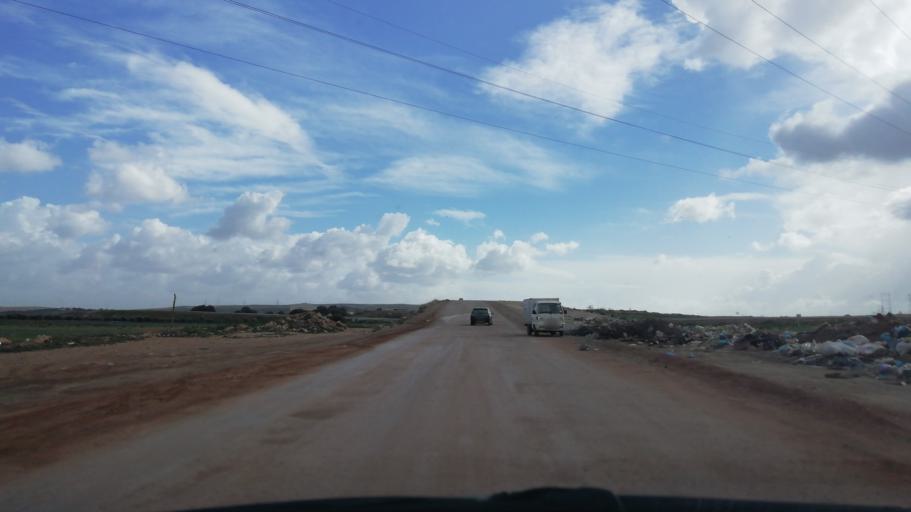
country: DZ
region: Oran
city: Sidi ech Chahmi
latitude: 35.6359
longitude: -0.5413
